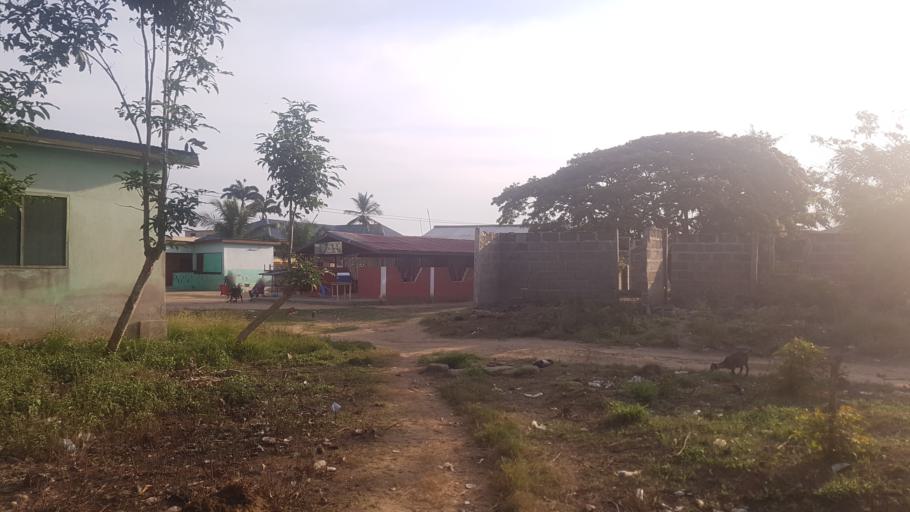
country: GH
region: Central
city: Winneba
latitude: 5.3545
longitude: -0.6303
